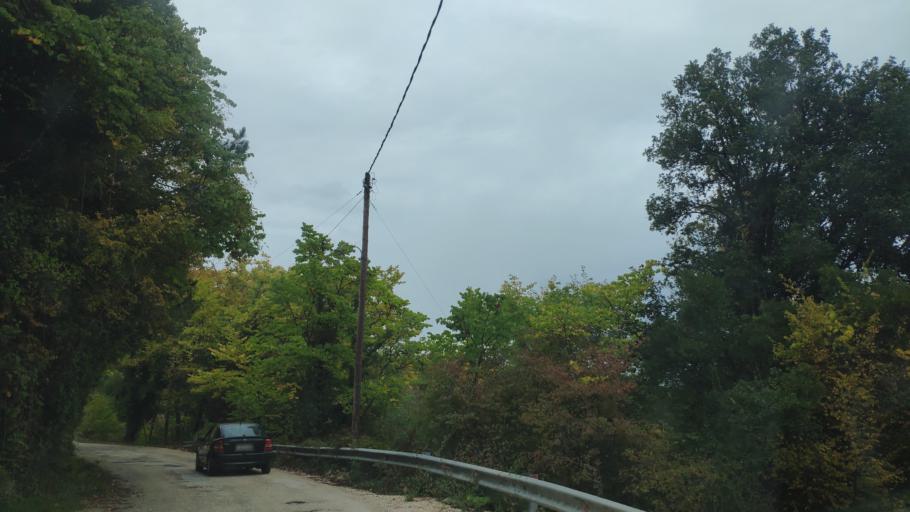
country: GR
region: Epirus
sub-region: Nomos Thesprotias
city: Paramythia
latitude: 39.4671
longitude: 20.6718
